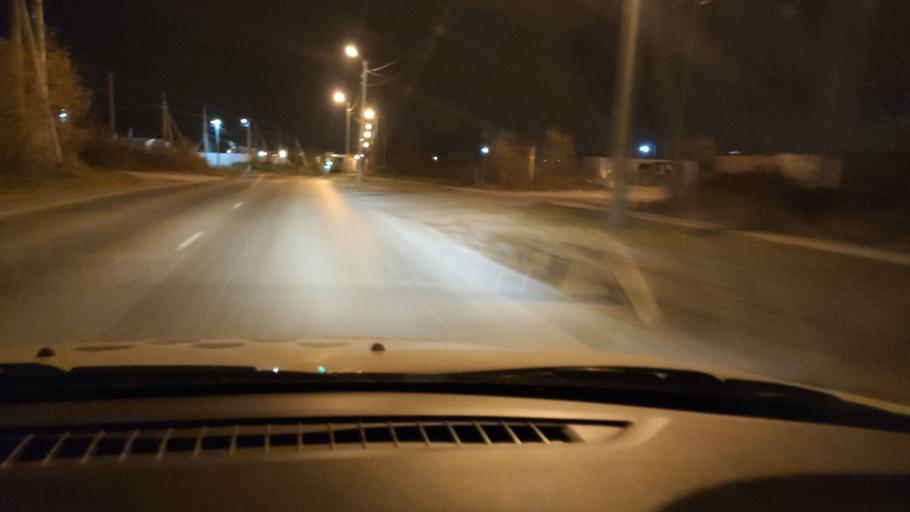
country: RU
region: Perm
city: Kondratovo
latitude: 57.9502
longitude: 56.1389
